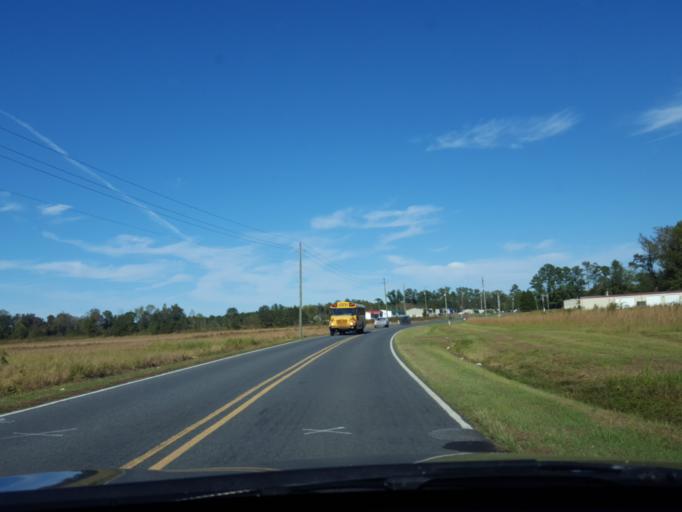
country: US
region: North Carolina
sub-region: Beaufort County
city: Washington
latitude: 35.6040
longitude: -77.1206
